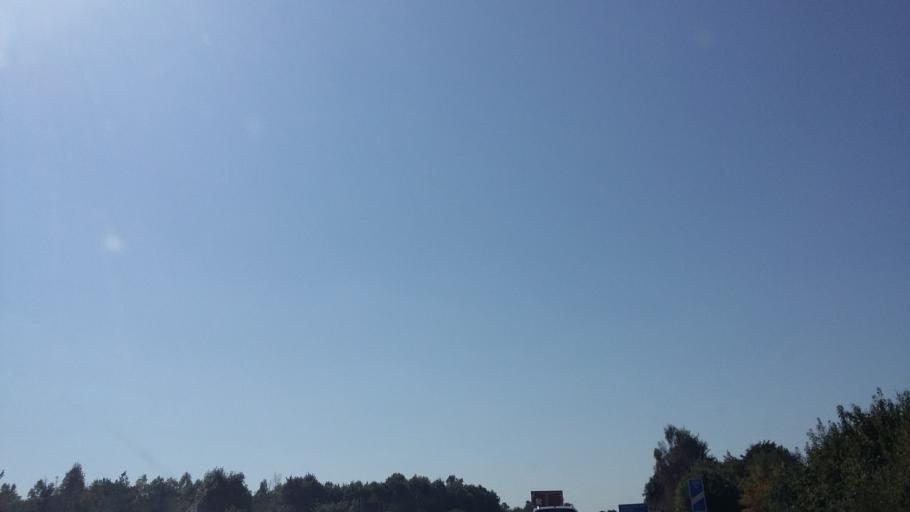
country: DE
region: Bavaria
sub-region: Upper Bavaria
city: Landsberg am Lech
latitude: 48.0530
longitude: 10.8435
